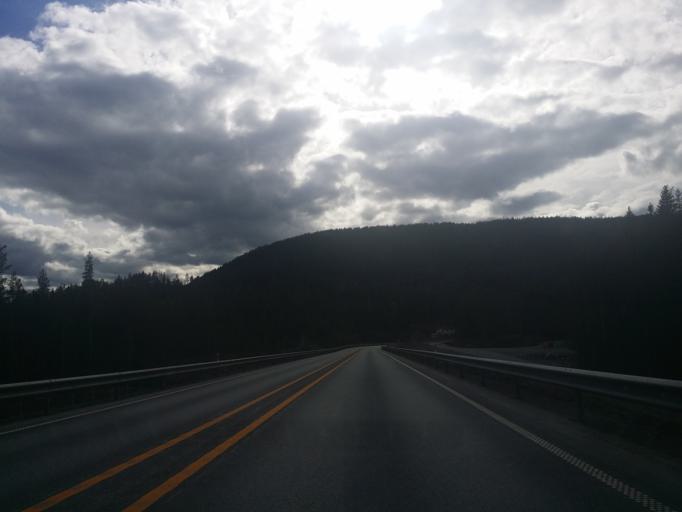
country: NO
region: Buskerud
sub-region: Krodsherad
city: Noresund
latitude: 60.2600
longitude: 9.8577
